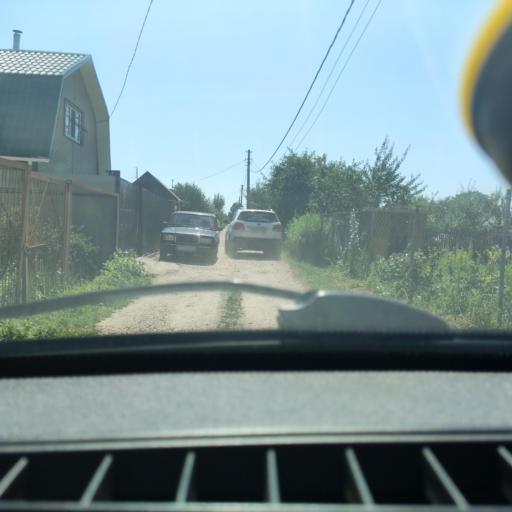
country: RU
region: Samara
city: Tol'yatti
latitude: 53.5986
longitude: 49.3063
